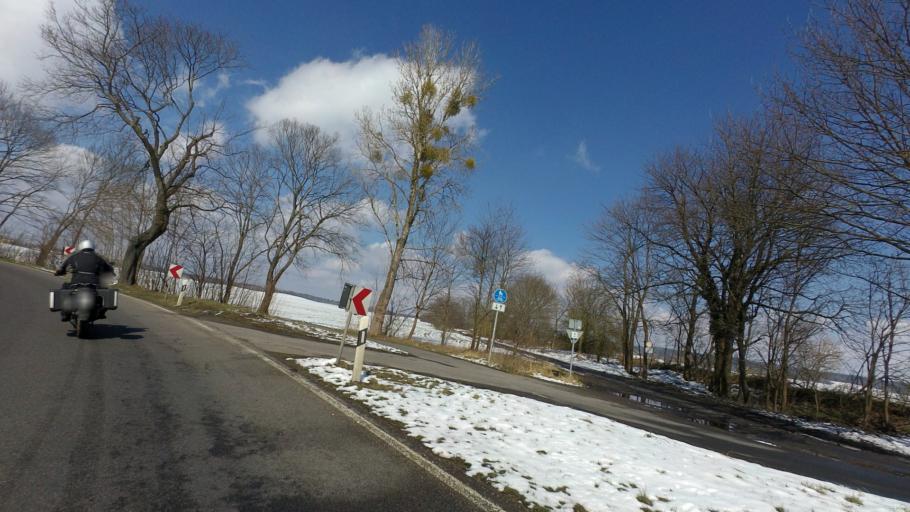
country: DE
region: Brandenburg
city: Britz
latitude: 52.8804
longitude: 13.7443
